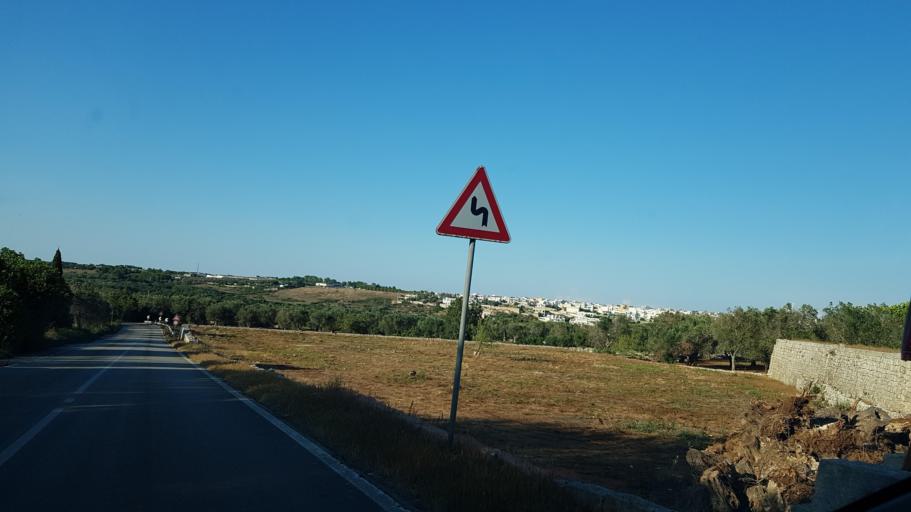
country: IT
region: Apulia
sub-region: Provincia di Lecce
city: Castro
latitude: 40.0037
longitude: 18.4145
